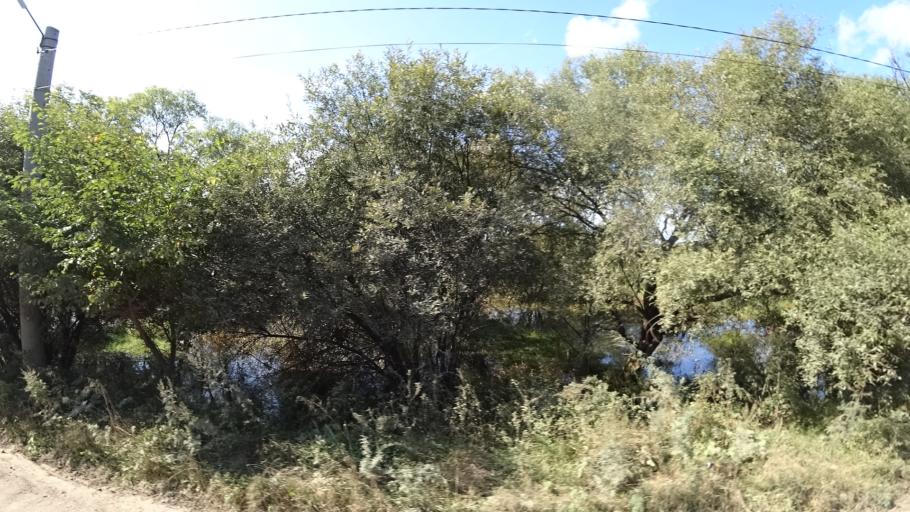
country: RU
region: Amur
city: Arkhara
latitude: 49.4028
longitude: 130.1520
